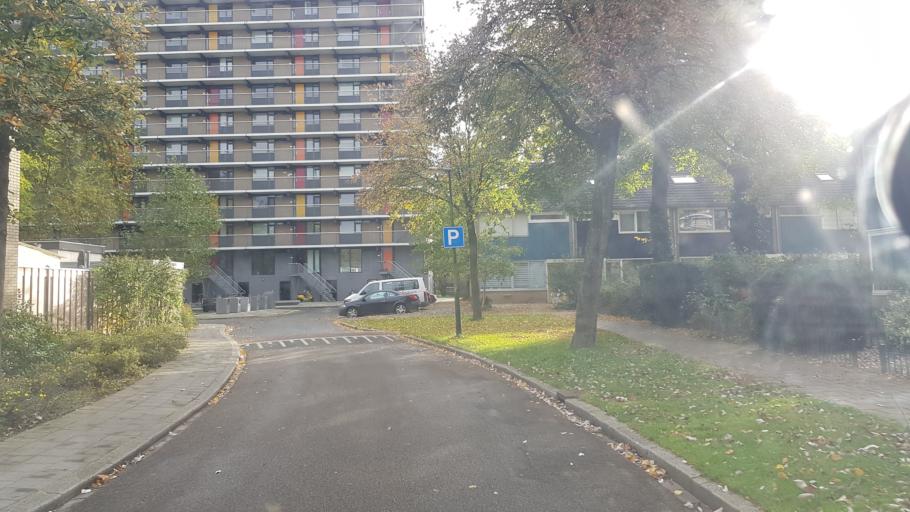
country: NL
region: Gelderland
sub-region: Gemeente Apeldoorn
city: Apeldoorn
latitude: 52.2275
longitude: 5.9831
